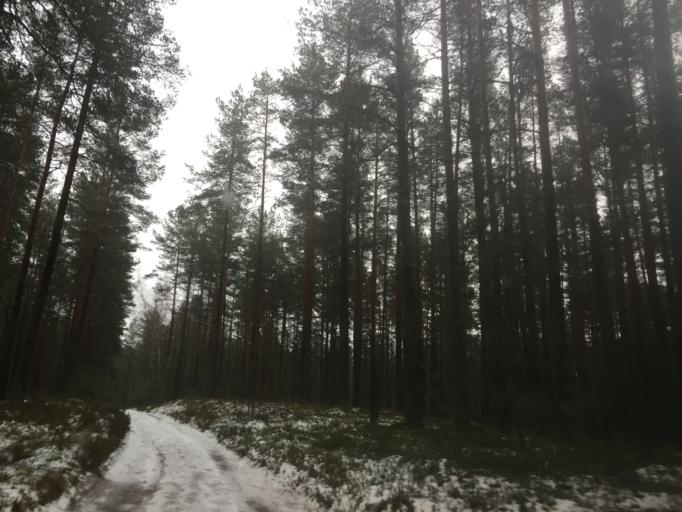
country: LV
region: Stopini
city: Ulbroka
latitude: 56.9544
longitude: 24.3347
